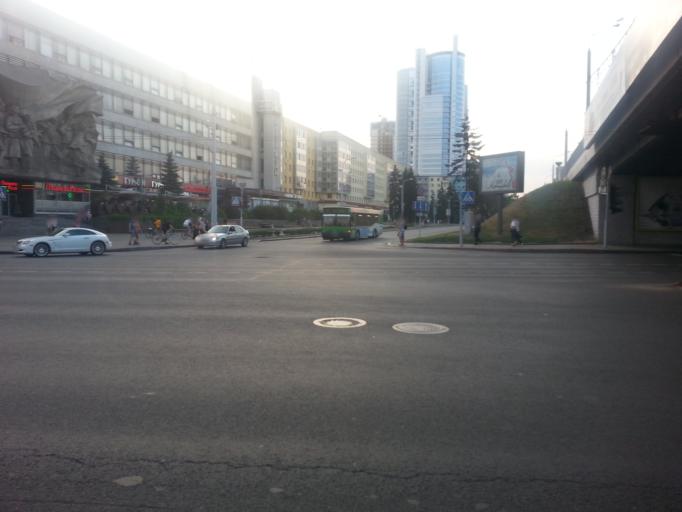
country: BY
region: Minsk
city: Minsk
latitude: 53.9049
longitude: 27.5532
